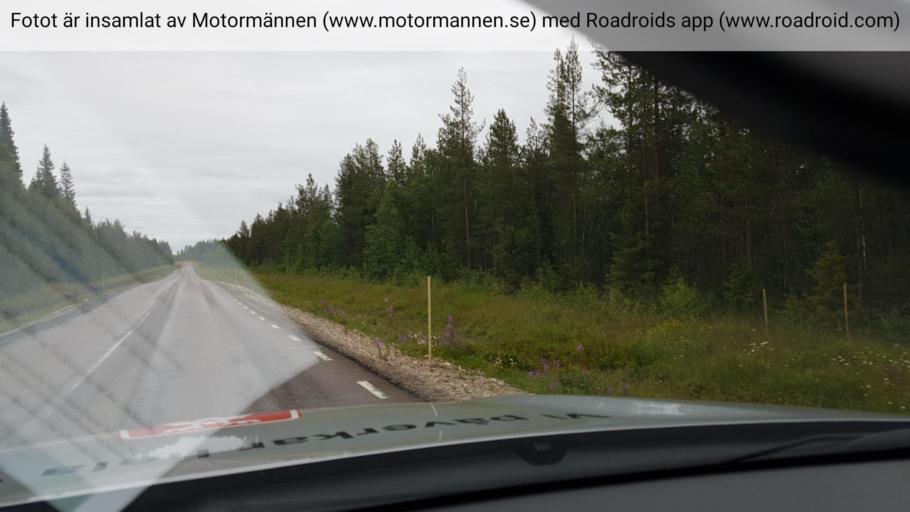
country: SE
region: Norrbotten
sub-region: Overkalix Kommun
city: OEverkalix
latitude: 67.0562
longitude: 22.3069
